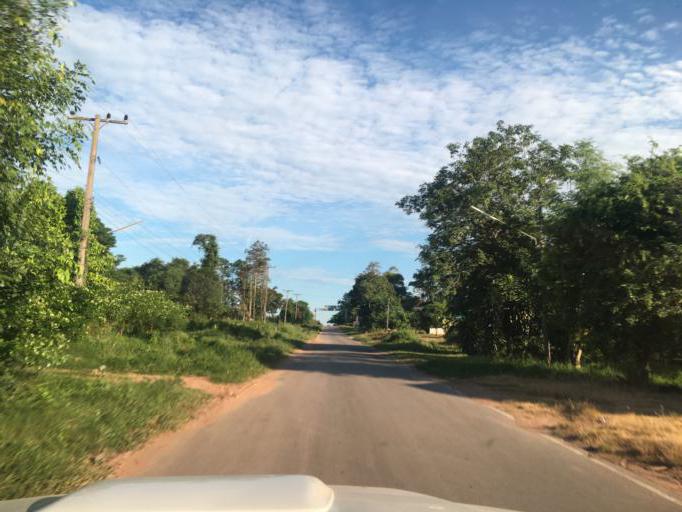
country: TH
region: Changwat Udon Thani
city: Kut Chap
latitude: 17.3108
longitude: 102.6624
